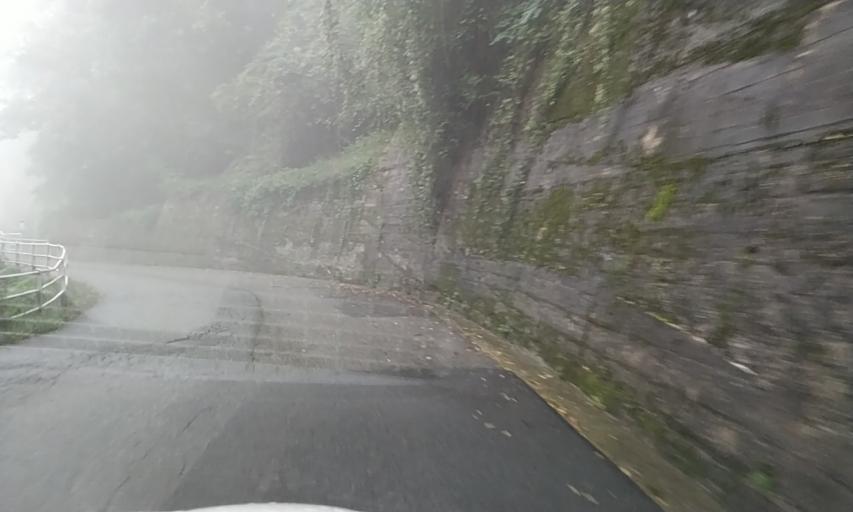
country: IT
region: Piedmont
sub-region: Provincia di Vercelli
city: Civiasco
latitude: 45.8301
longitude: 8.2813
